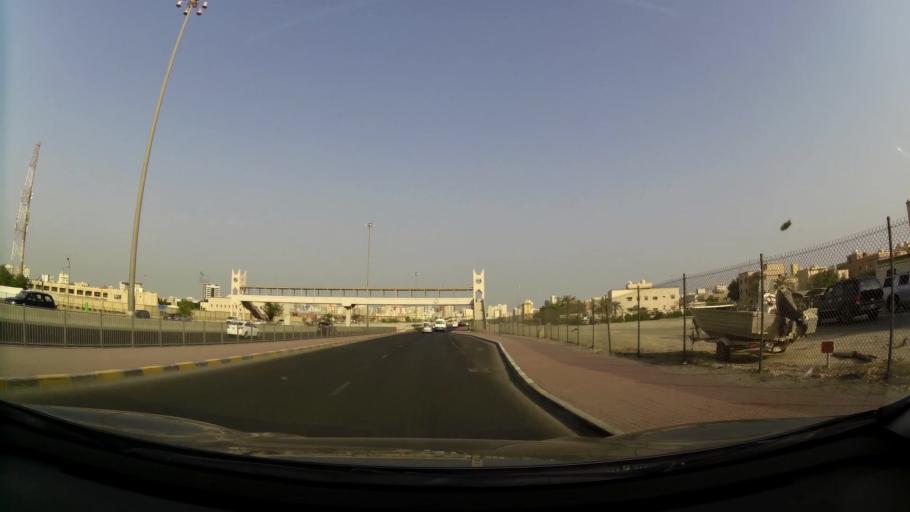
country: KW
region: Muhafazat Hawalli
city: As Salimiyah
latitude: 29.3255
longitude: 48.0744
